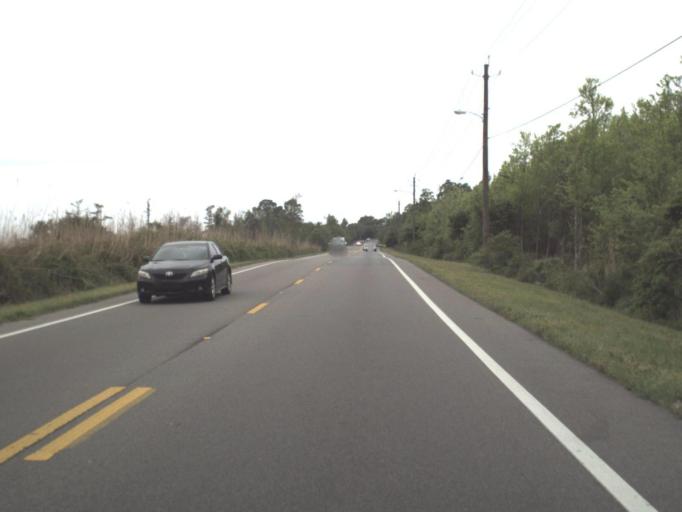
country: US
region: Florida
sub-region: Escambia County
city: East Pensacola Heights
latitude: 30.4759
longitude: -87.1629
